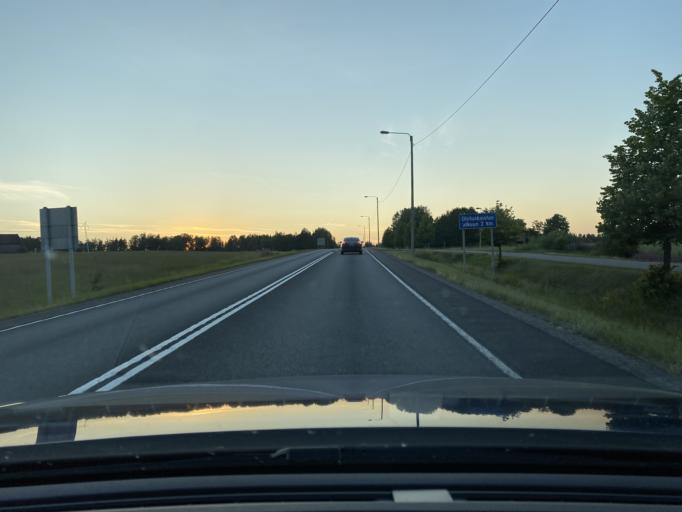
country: FI
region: Pirkanmaa
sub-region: Luoteis-Pirkanmaa
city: Ikaalinen
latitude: 61.7613
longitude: 23.0245
